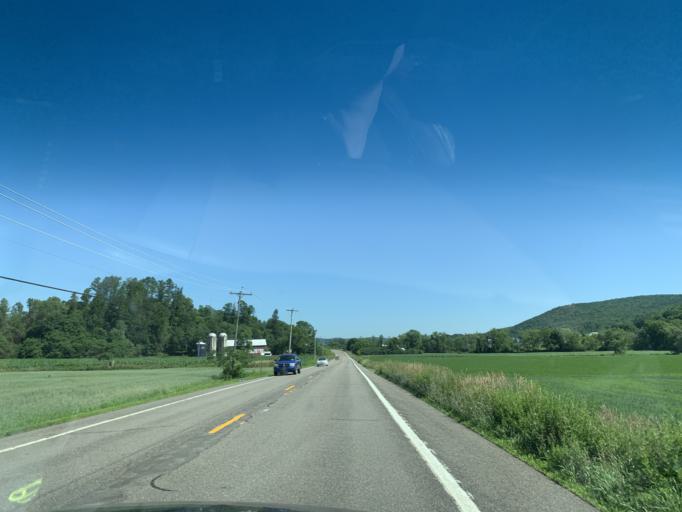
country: US
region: New York
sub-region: Chenango County
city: Norwich
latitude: 42.4915
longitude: -75.4007
